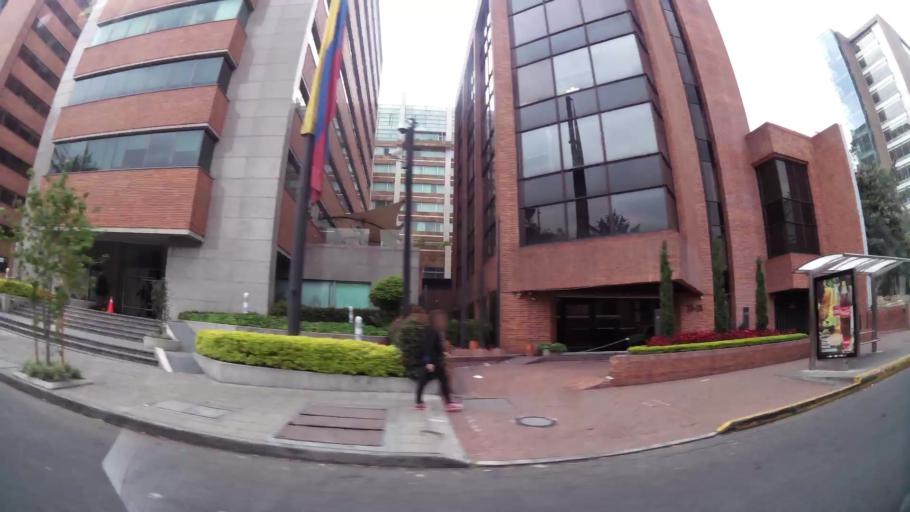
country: CO
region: Bogota D.C.
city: Barrio San Luis
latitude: 4.6575
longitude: -74.0559
